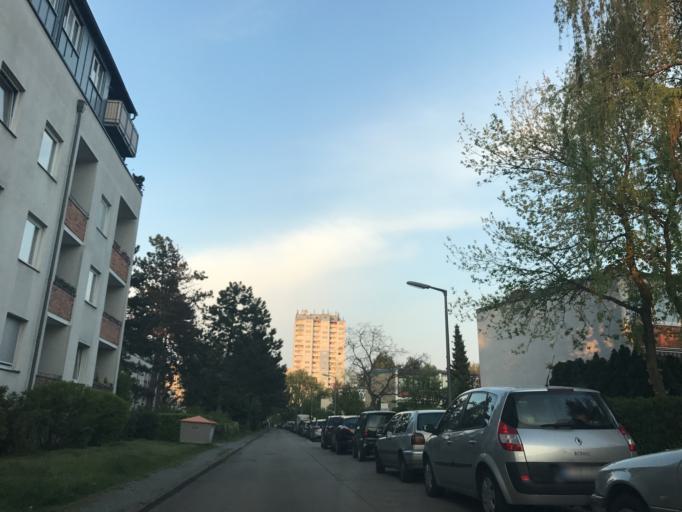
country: DE
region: Berlin
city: Staaken
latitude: 52.5313
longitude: 13.1598
